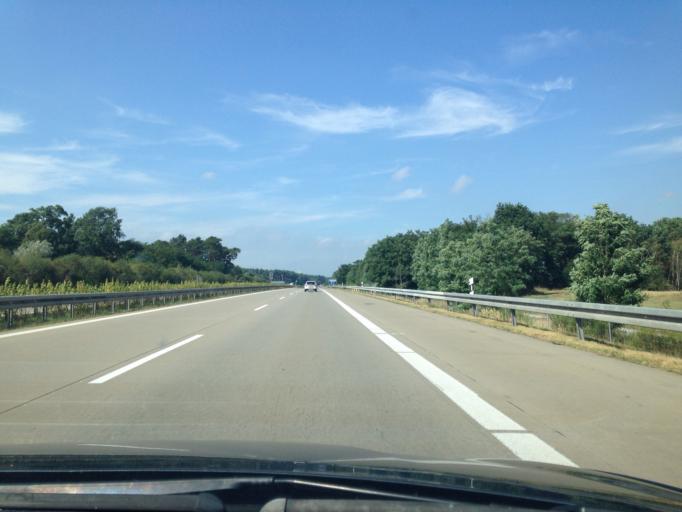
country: DE
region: Brandenburg
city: Luebben
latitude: 51.8870
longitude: 13.8483
